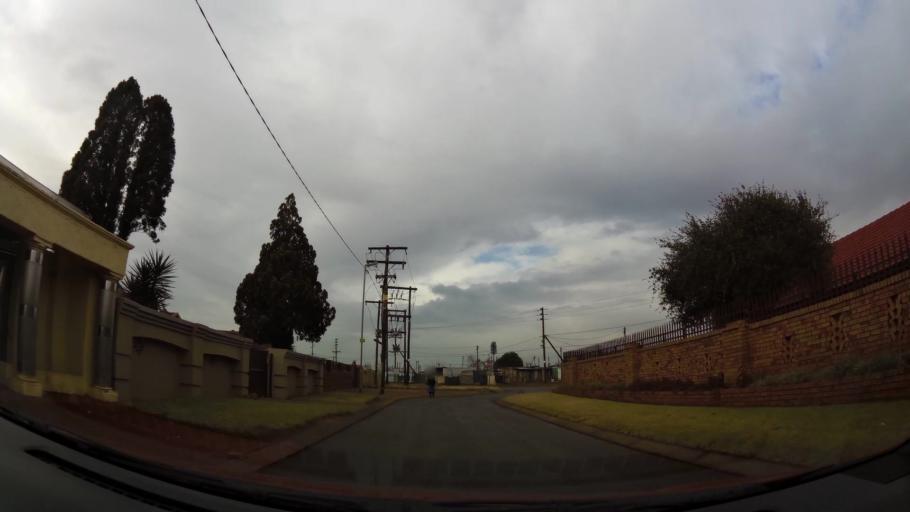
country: ZA
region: Gauteng
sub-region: City of Johannesburg Metropolitan Municipality
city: Soweto
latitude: -26.2899
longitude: 27.8400
